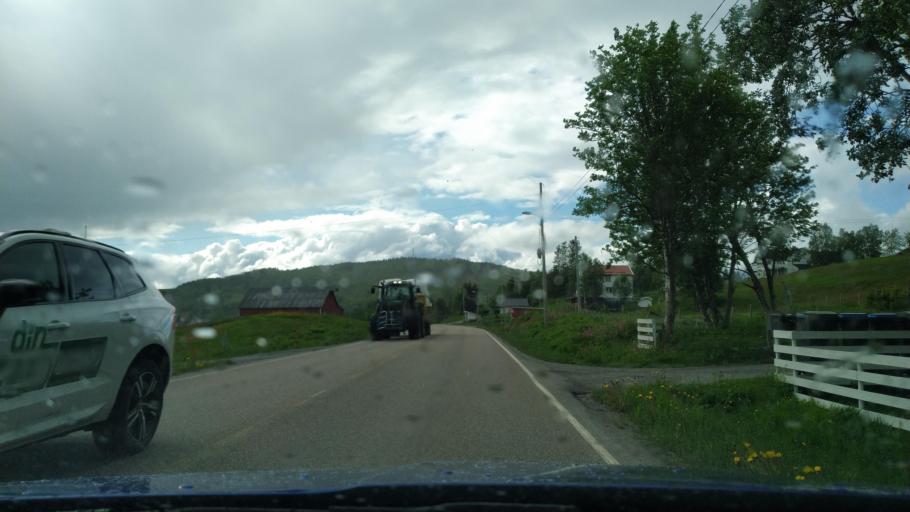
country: NO
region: Troms
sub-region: Sorreisa
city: Sorreisa
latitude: 69.1609
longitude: 18.1231
